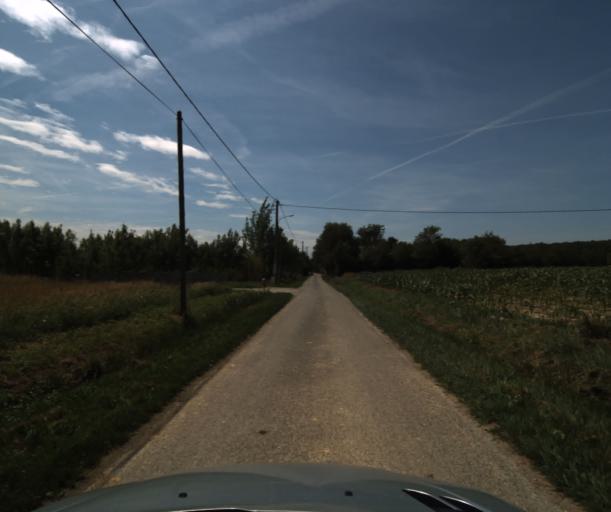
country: FR
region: Midi-Pyrenees
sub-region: Departement de la Haute-Garonne
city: Labastidette
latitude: 43.4479
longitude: 1.2390
